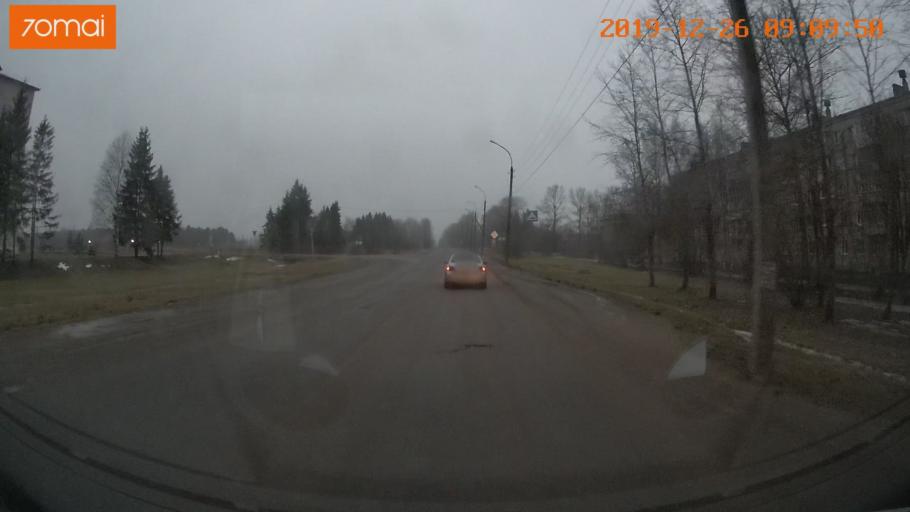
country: RU
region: Vologda
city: Gryazovets
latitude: 58.8670
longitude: 40.2527
